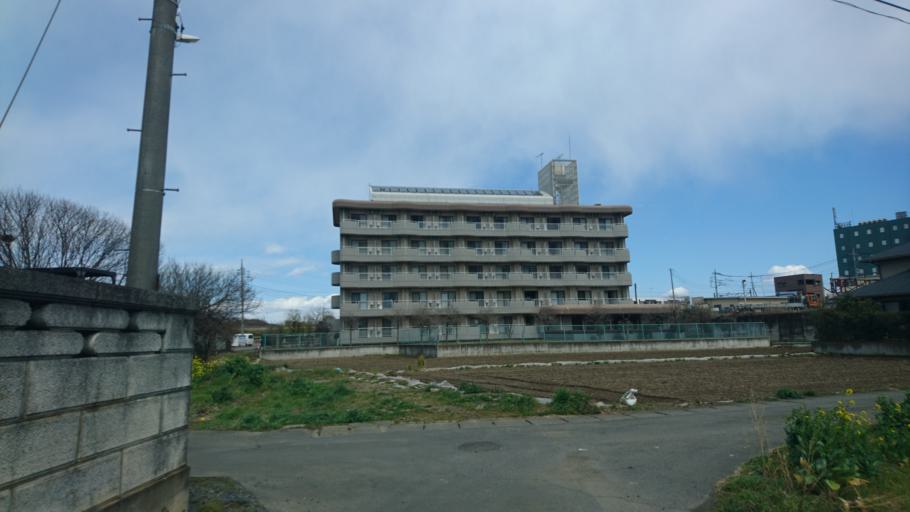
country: JP
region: Ibaraki
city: Yuki
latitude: 36.2950
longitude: 139.9125
